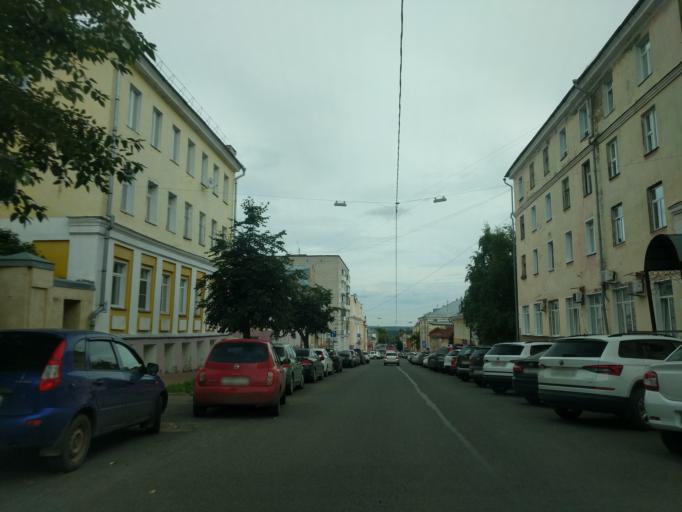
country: RU
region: Kirov
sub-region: Kirovo-Chepetskiy Rayon
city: Kirov
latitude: 58.6020
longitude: 49.6751
